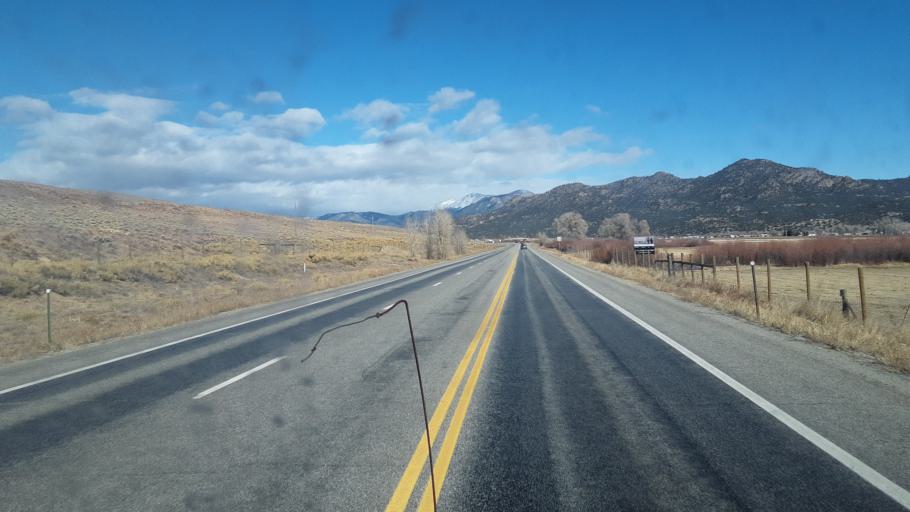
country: US
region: Colorado
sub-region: Chaffee County
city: Buena Vista
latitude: 38.7969
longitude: -106.1144
